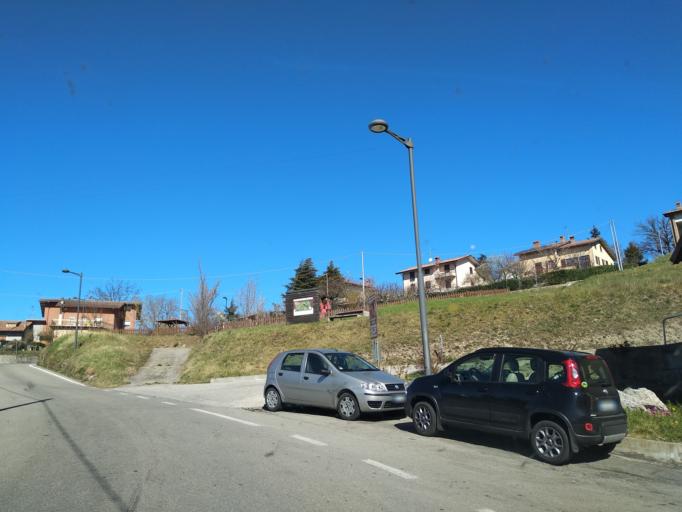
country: IT
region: Emilia-Romagna
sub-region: Provincia di Reggio Emilia
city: Castelnovo ne'Monti
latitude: 44.4139
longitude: 10.4021
